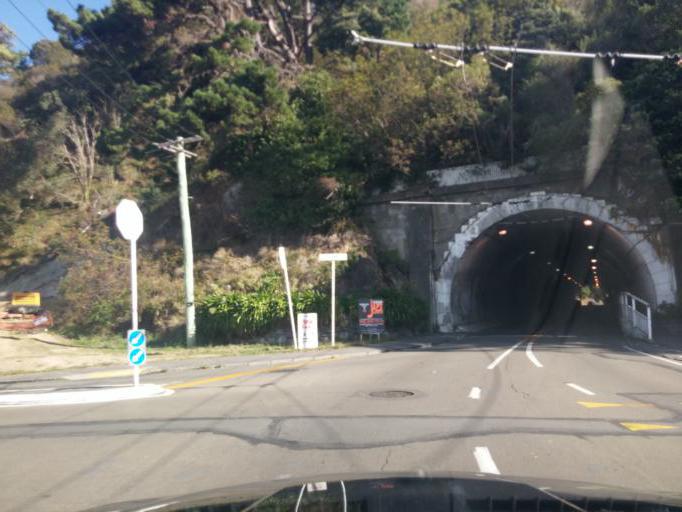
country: NZ
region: Wellington
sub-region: Wellington City
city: Wellington
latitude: -41.3231
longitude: 174.8287
